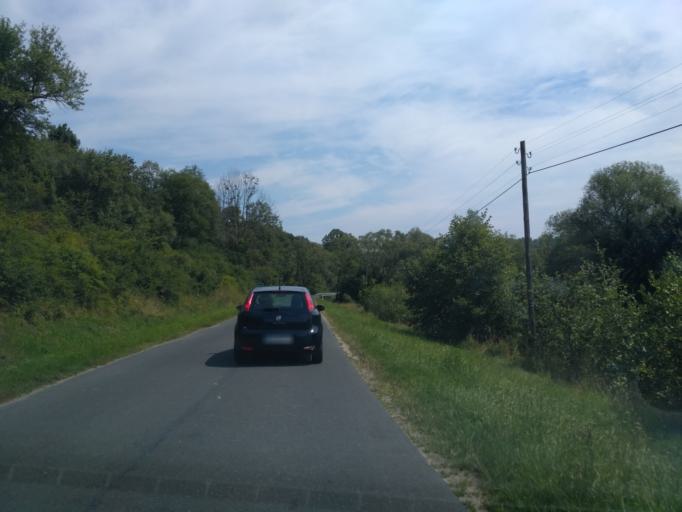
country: PL
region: Subcarpathian Voivodeship
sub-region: Powiat bieszczadzki
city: Czarna
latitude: 49.3029
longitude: 22.5489
